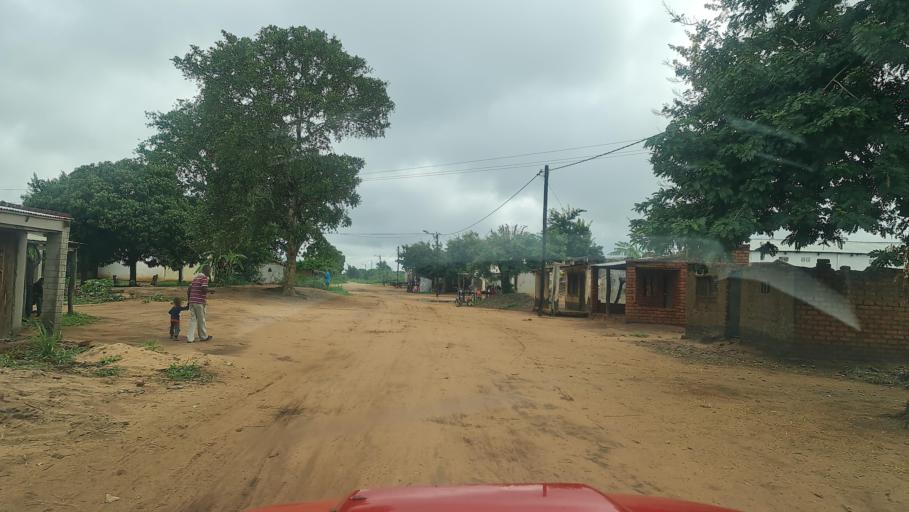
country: MW
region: Southern Region
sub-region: Nsanje District
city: Nsanje
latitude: -17.1905
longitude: 35.7083
